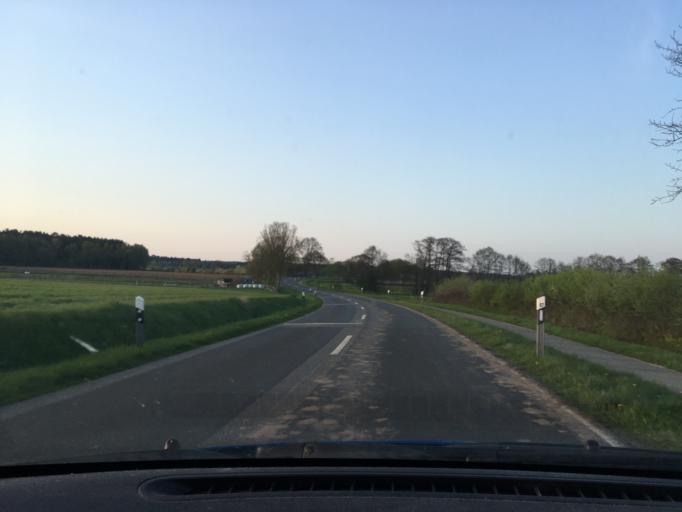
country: DE
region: Lower Saxony
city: Kirchgellersen
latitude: 53.2356
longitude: 10.2980
